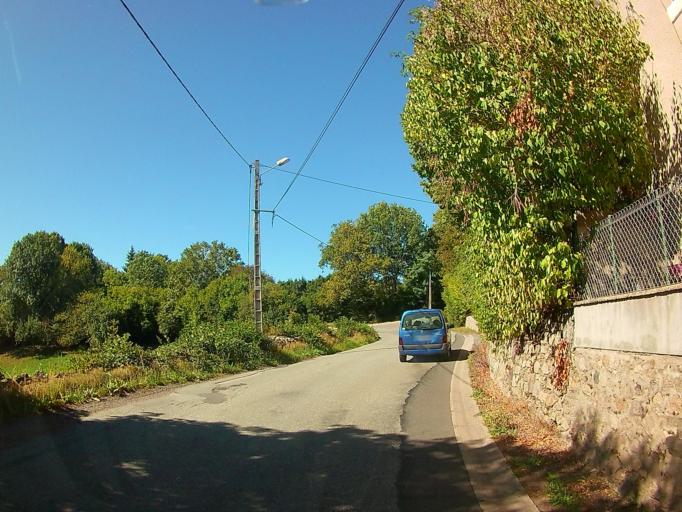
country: FR
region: Auvergne
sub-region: Departement du Puy-de-Dome
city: Manzat
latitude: 45.9109
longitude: 2.9354
